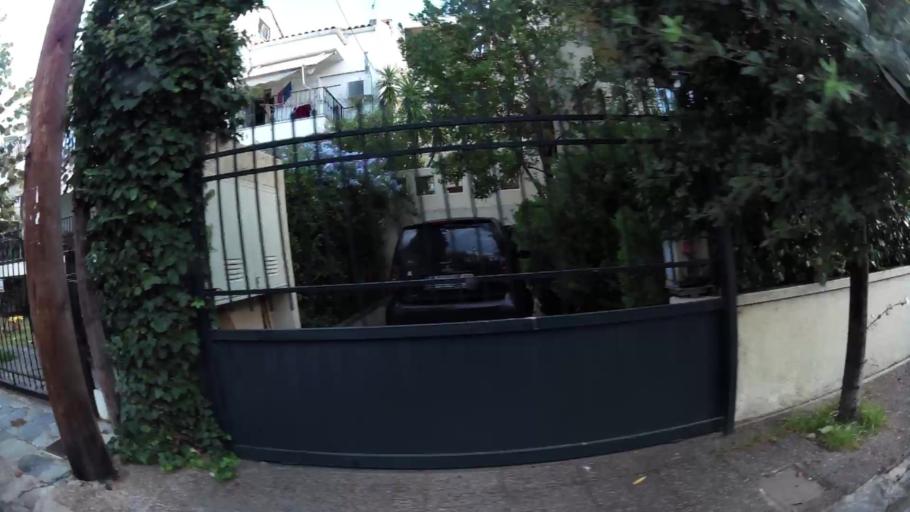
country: GR
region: Attica
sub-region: Nomarchia Athinas
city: Vrilissia
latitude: 38.0396
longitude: 23.8233
